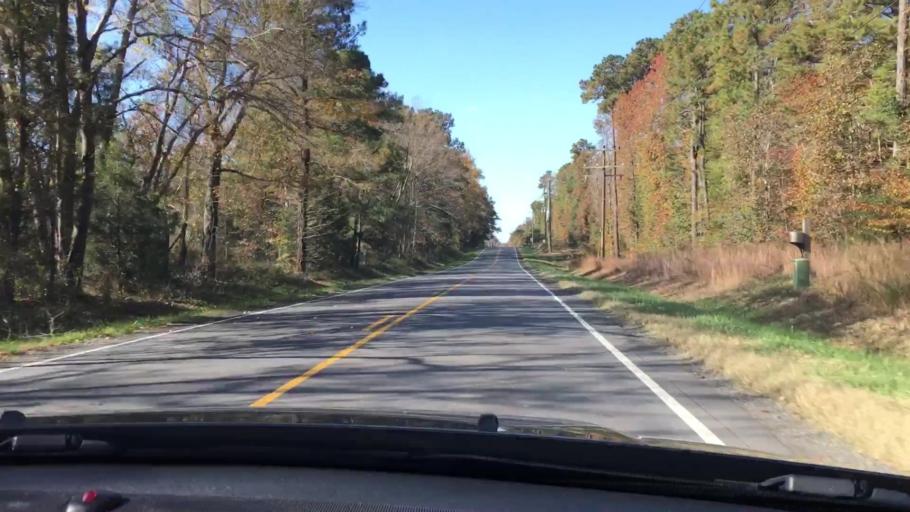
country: US
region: Virginia
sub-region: King William County
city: King William
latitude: 37.7003
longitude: -77.0420
